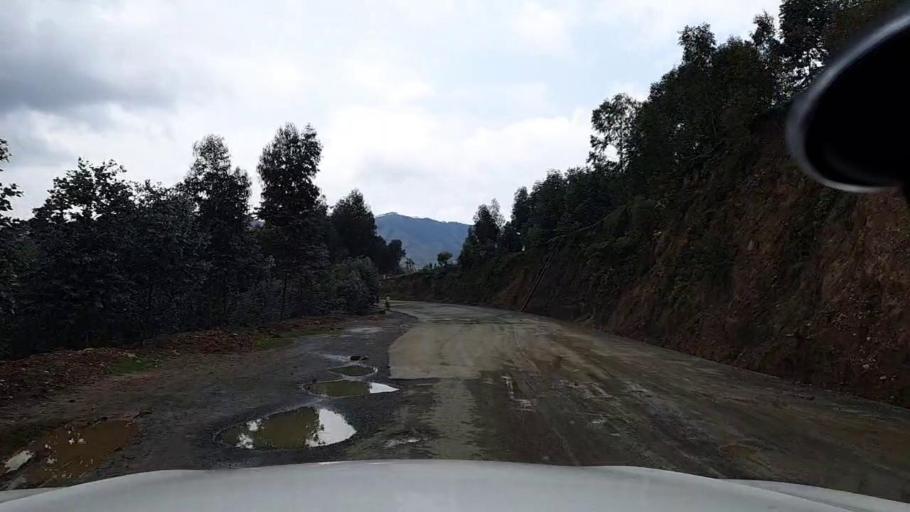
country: RW
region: Western Province
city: Kibuye
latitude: -2.0590
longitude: 29.5252
